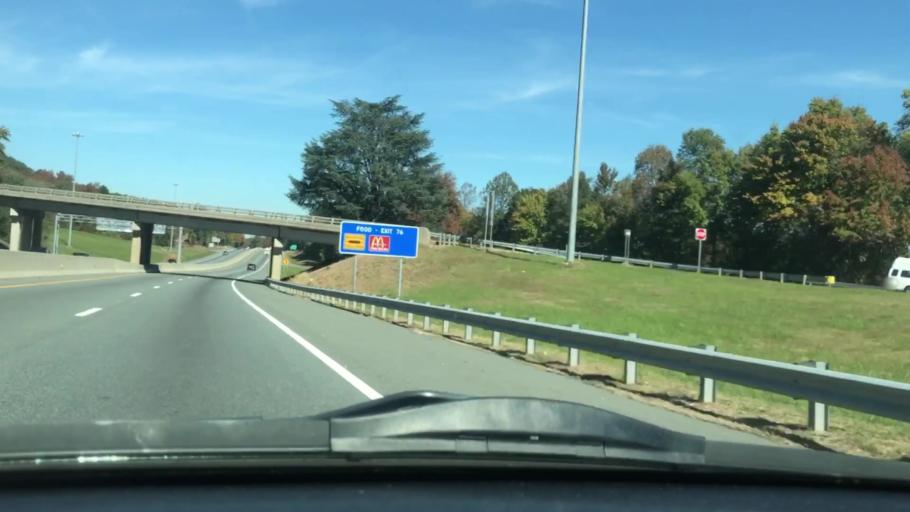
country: US
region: North Carolina
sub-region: Randolph County
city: Asheboro
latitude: 35.7190
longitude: -79.8263
